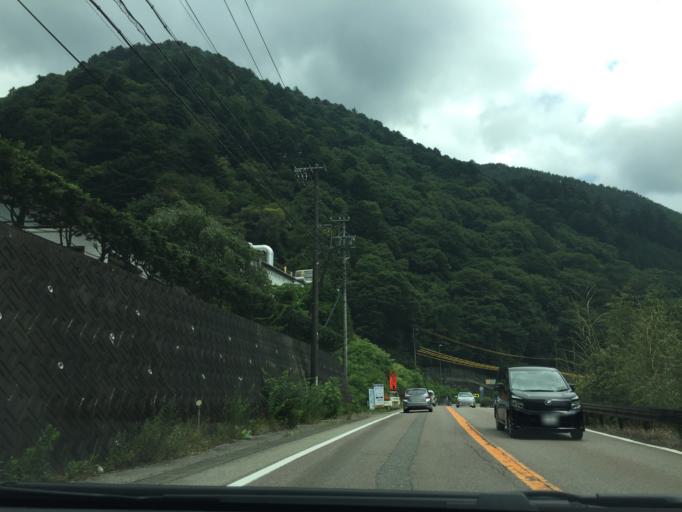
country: JP
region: Gifu
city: Gujo
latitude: 35.7769
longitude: 137.2222
